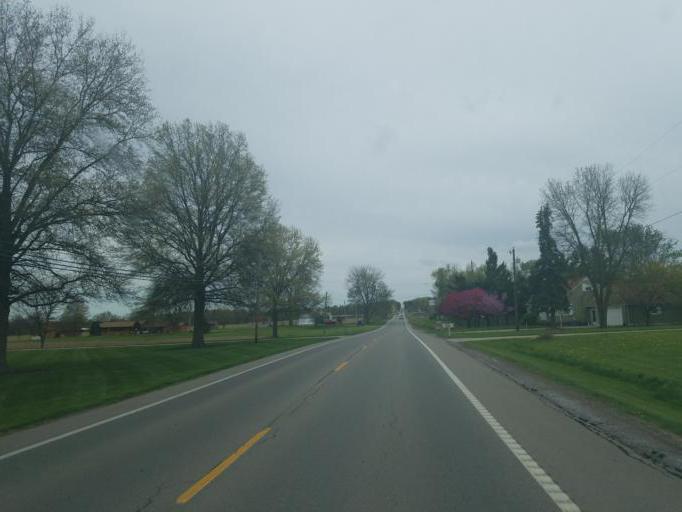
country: US
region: Ohio
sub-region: Wayne County
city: Orrville
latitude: 40.8157
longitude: -81.7653
